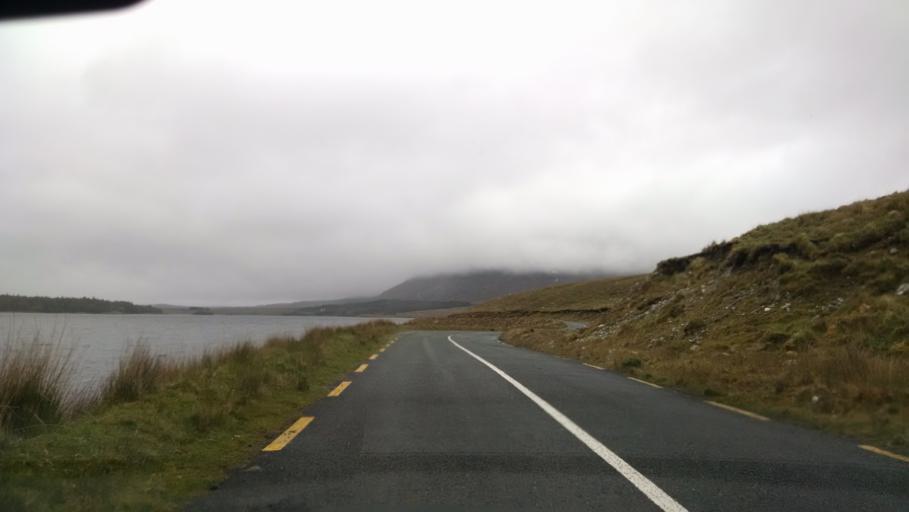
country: IE
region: Connaught
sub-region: County Galway
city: Clifden
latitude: 53.4985
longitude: -9.7357
